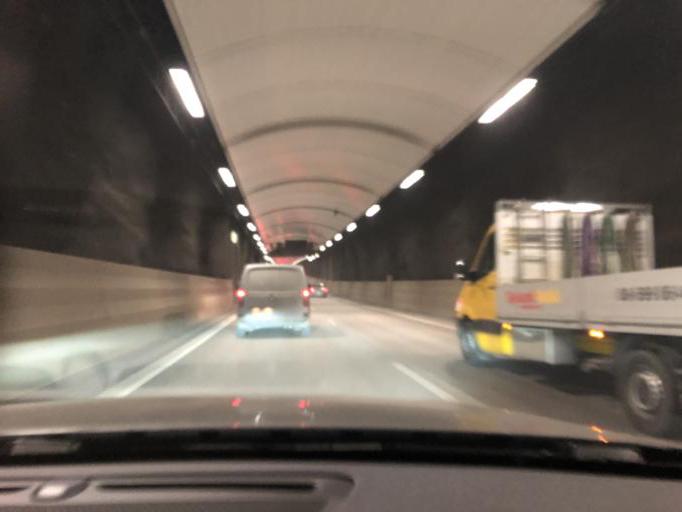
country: SE
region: Stockholm
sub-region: Stockholms Kommun
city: Arsta
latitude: 59.2920
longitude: 18.0618
